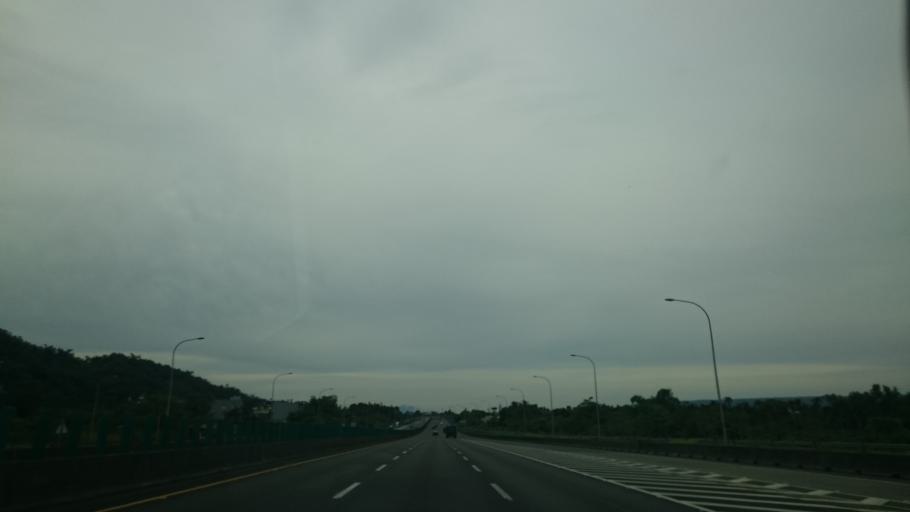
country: TW
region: Taiwan
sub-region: Nantou
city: Nantou
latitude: 23.8749
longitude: 120.7067
